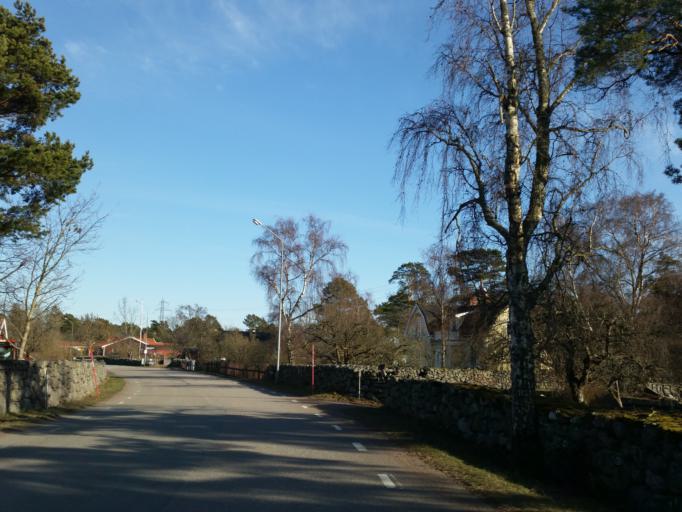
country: SE
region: Kalmar
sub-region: Kalmar Kommun
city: Lindsdal
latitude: 56.7797
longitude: 16.4122
